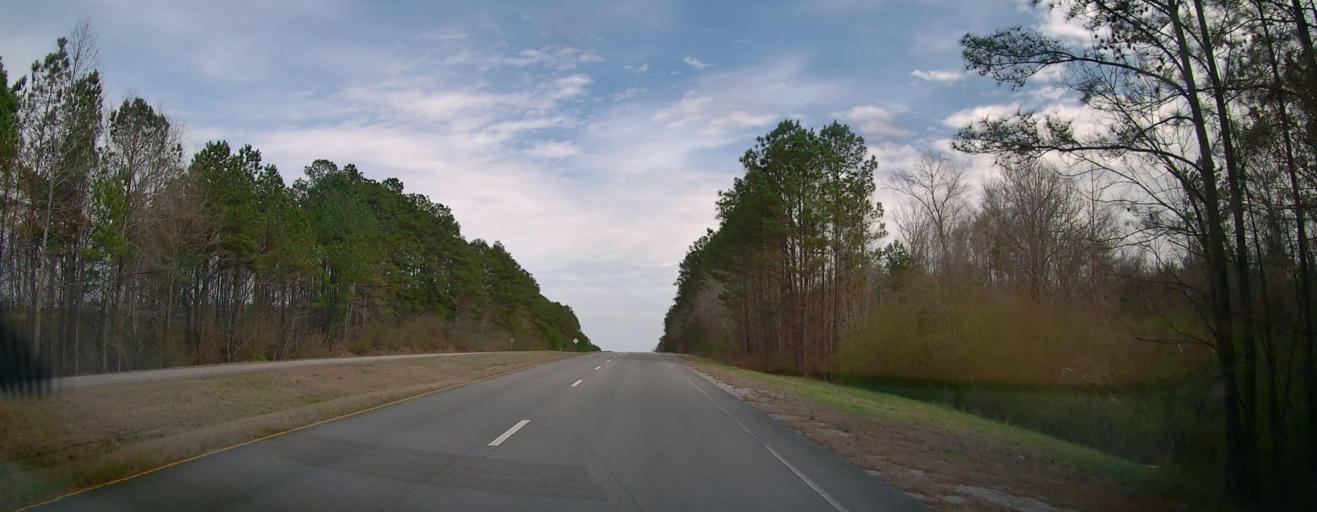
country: US
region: Alabama
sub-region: Marion County
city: Winfield
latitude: 33.9322
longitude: -87.7010
